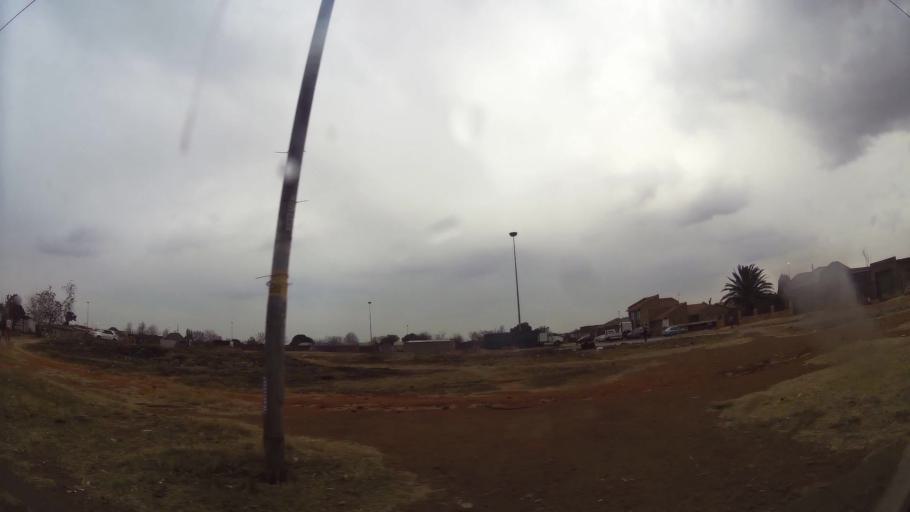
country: ZA
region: Gauteng
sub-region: Ekurhuleni Metropolitan Municipality
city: Germiston
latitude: -26.3469
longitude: 28.1441
